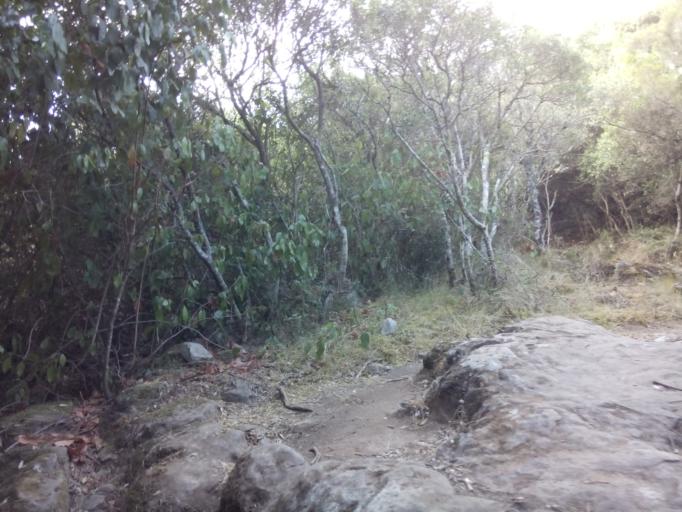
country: FR
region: Corsica
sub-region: Departement de la Corse-du-Sud
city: Sari-Solenzara
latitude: 41.8303
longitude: 9.3664
